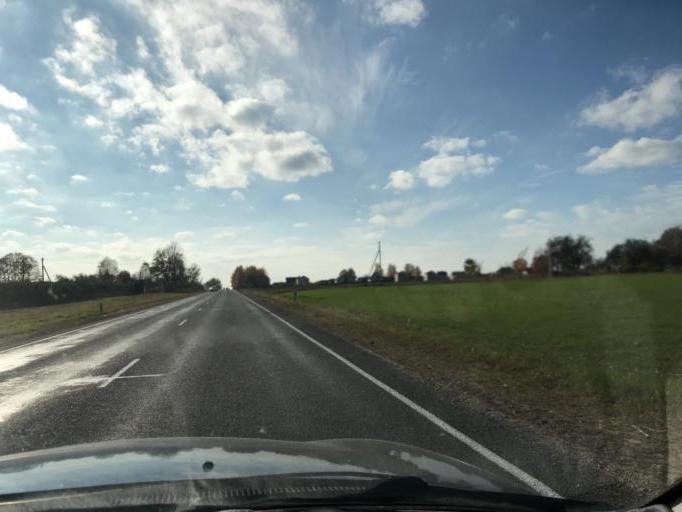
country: BY
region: Grodnenskaya
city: Voranava
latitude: 54.1706
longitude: 25.3320
